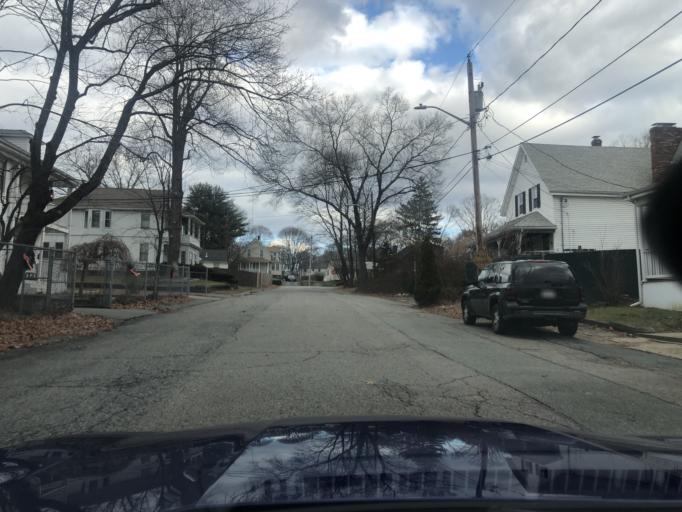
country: US
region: Massachusetts
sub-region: Norfolk County
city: Avon
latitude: 42.1123
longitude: -71.0199
